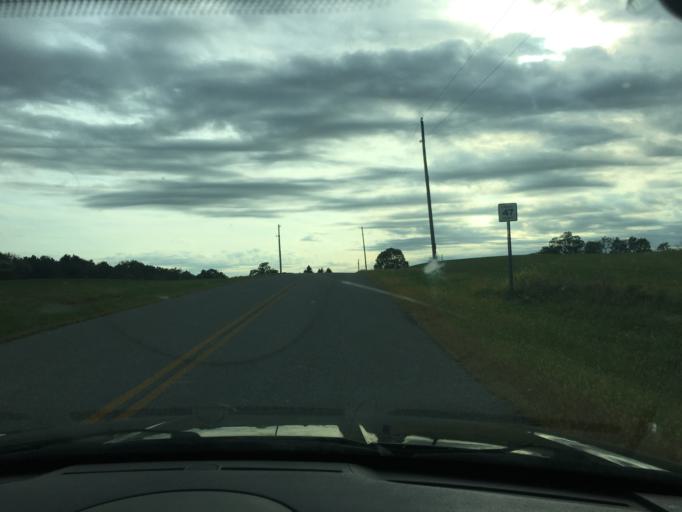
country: US
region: Ohio
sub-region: Logan County
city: West Liberty
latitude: 40.2840
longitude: -83.6939
